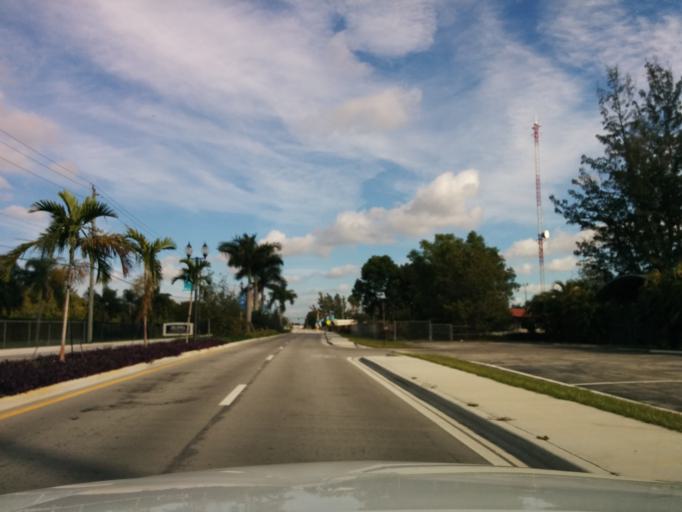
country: US
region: Florida
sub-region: Broward County
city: Davie
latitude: 26.0847
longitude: -80.2369
